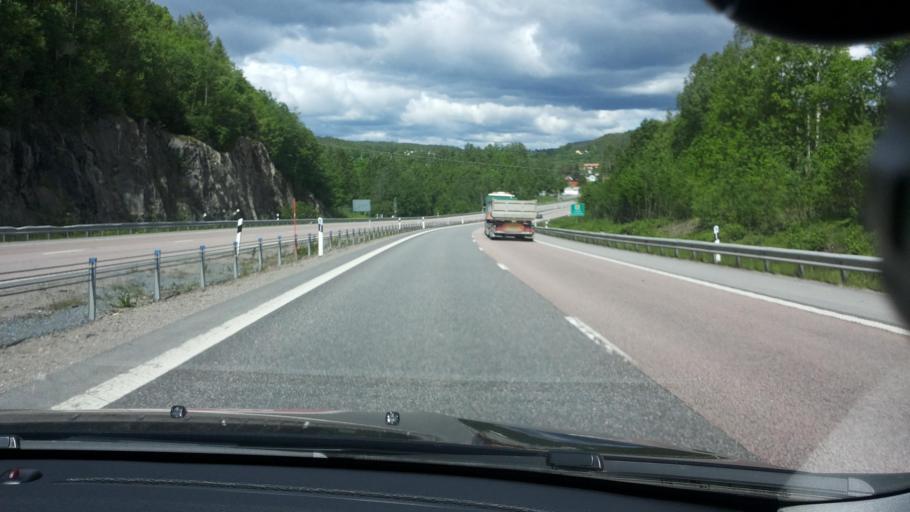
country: SE
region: Vaesternorrland
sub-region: Timra Kommun
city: Timra
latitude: 62.4693
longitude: 17.3175
